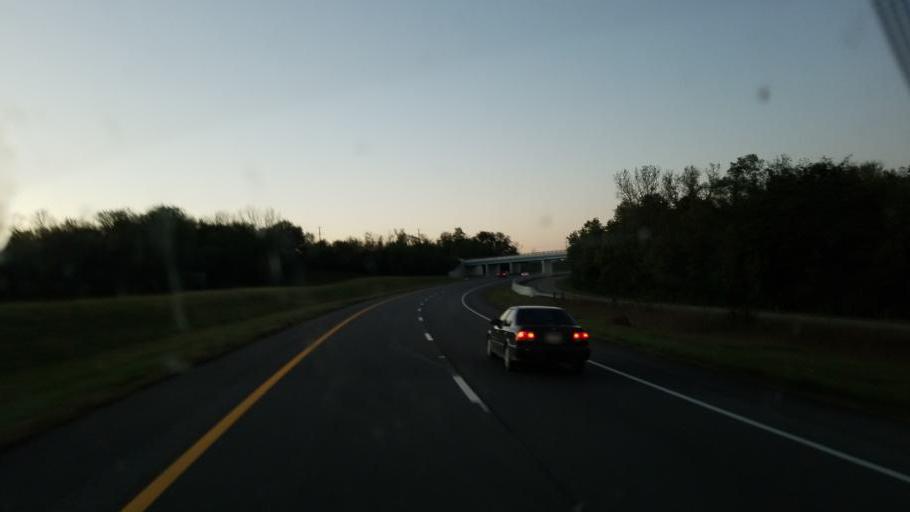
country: US
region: Ohio
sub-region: Ross County
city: Chillicothe
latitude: 39.3510
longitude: -82.9638
